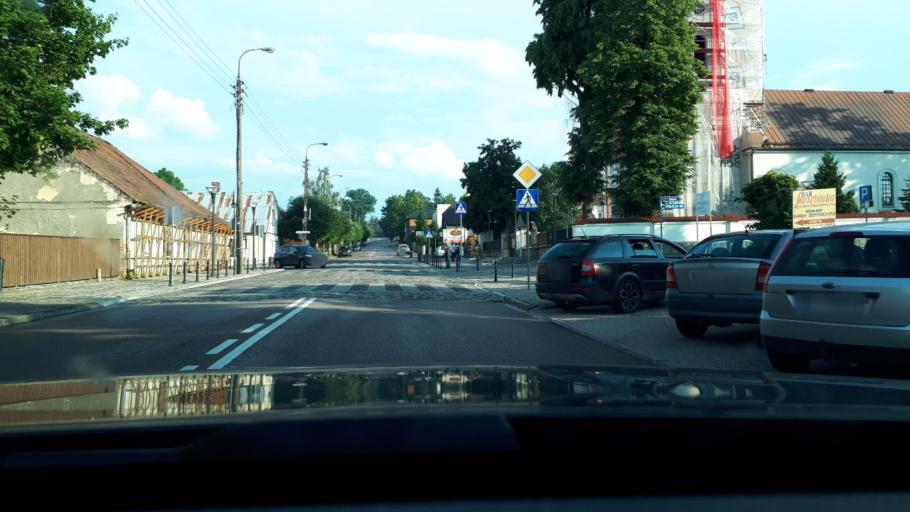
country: PL
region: Podlasie
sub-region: Powiat bialostocki
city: Suprasl
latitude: 53.2061
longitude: 23.3380
